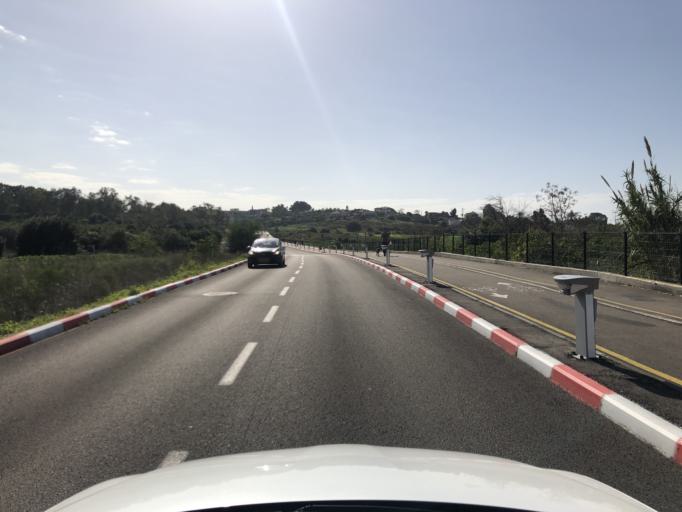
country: IL
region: Central District
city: Ness Ziona
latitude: 31.9204
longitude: 34.7852
